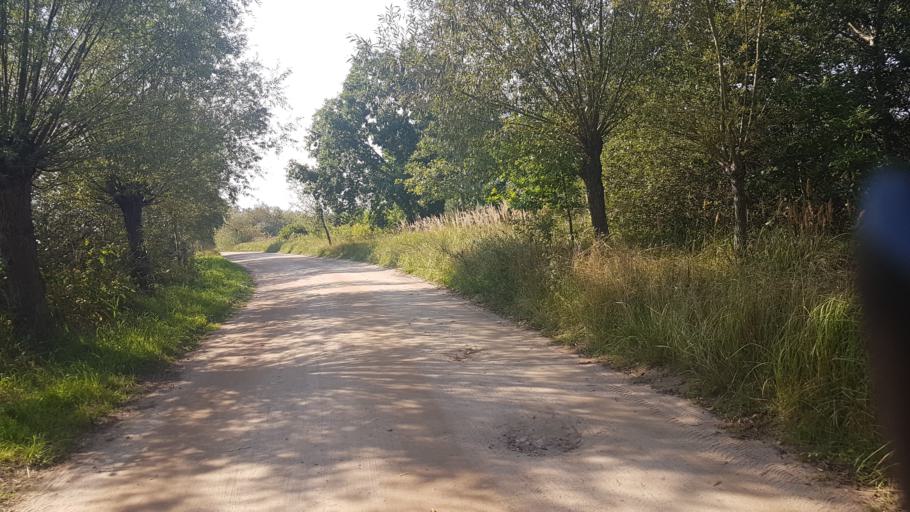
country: DE
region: Mecklenburg-Vorpommern
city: Putbus
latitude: 54.3315
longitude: 13.4661
